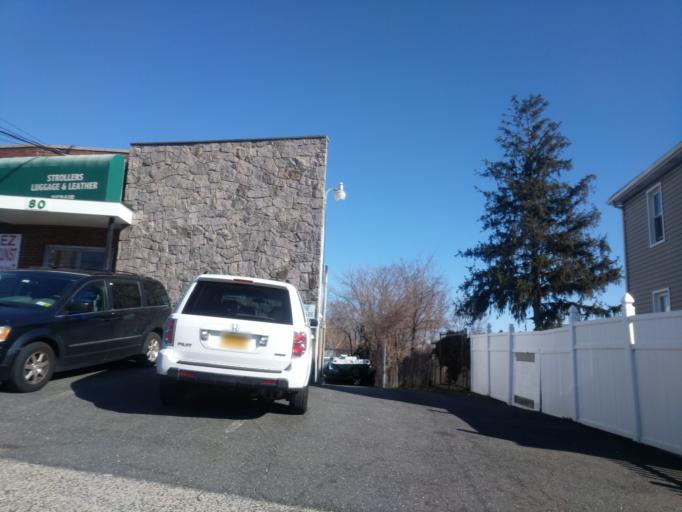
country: US
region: New York
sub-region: Nassau County
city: Inwood
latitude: 40.6186
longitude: -73.7400
